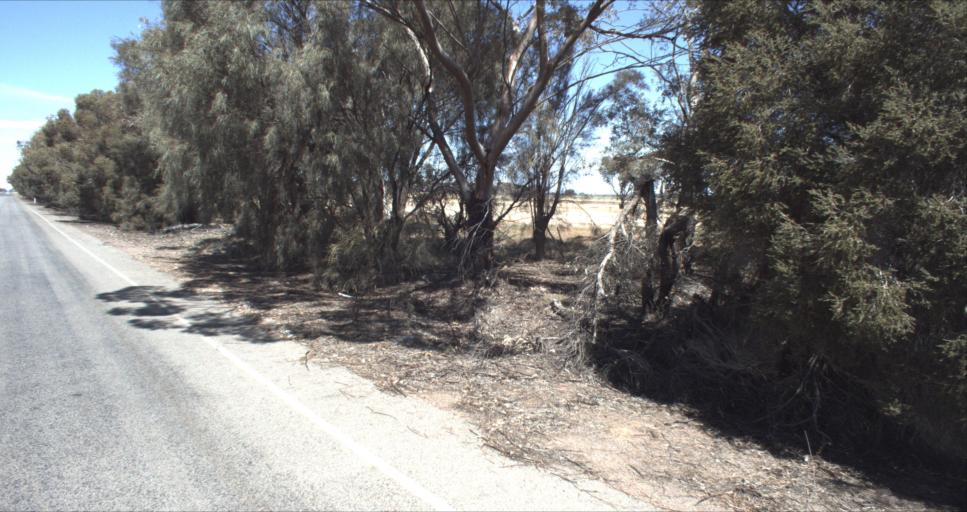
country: AU
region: New South Wales
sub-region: Leeton
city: Leeton
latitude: -34.4691
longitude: 146.2927
